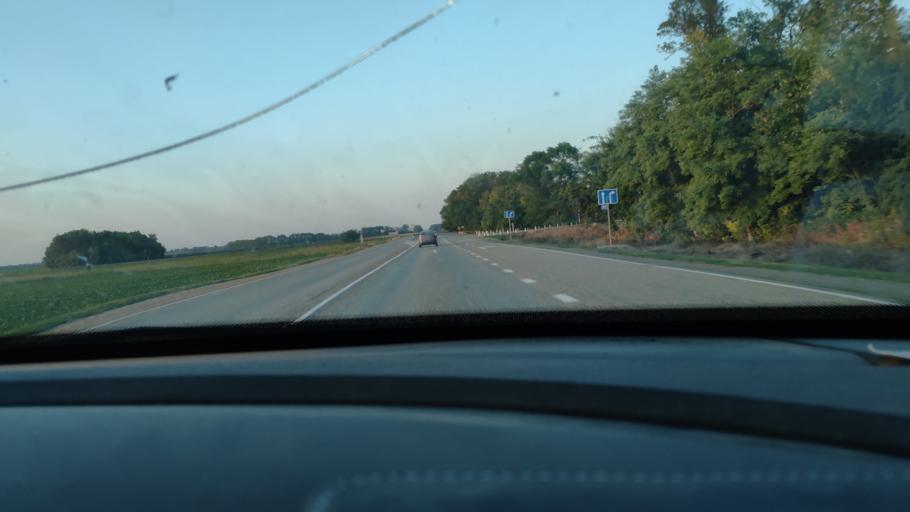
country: RU
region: Krasnodarskiy
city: Starominskaya
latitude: 46.4628
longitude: 39.0386
